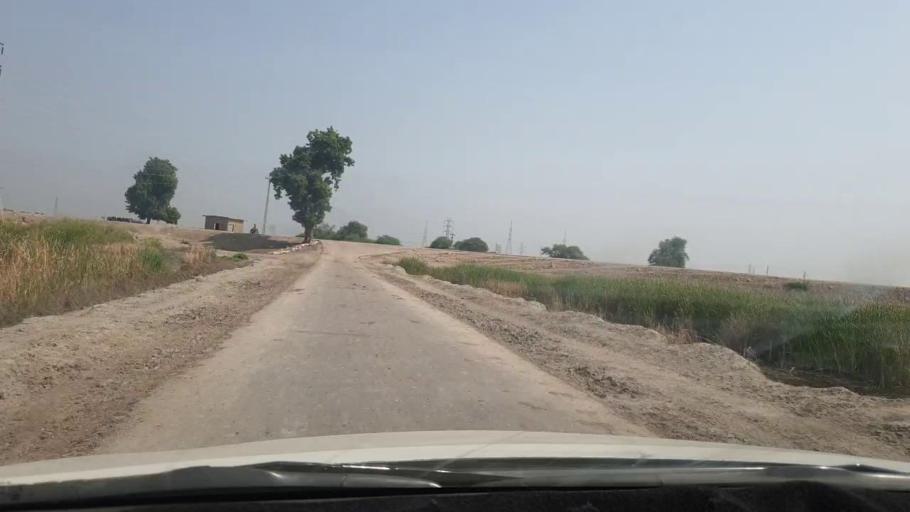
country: PK
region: Sindh
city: Rohri
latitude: 27.6374
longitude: 68.8841
